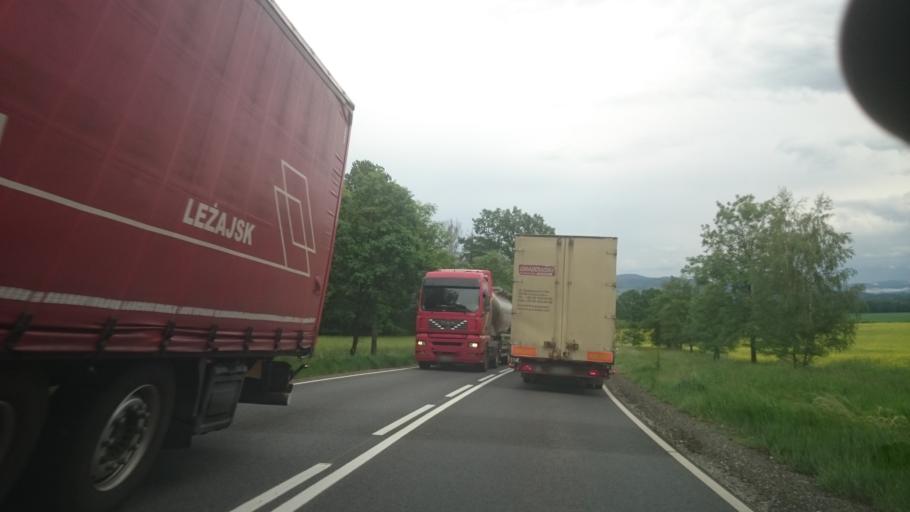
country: PL
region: Lower Silesian Voivodeship
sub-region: Powiat klodzki
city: Klodzko
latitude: 50.4318
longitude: 16.7137
